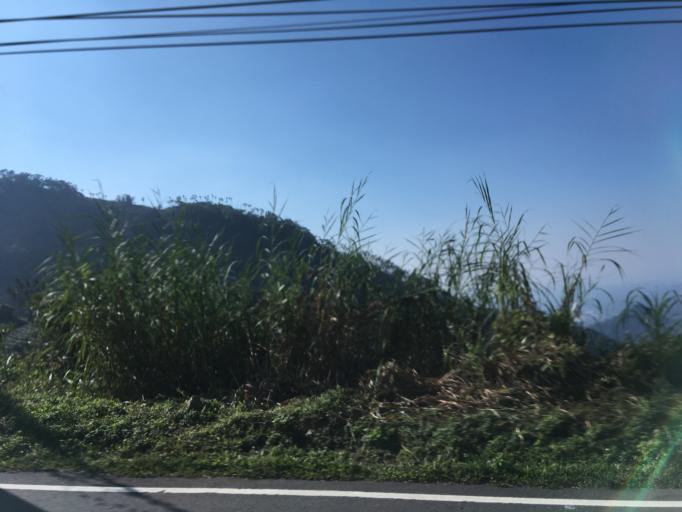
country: TW
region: Taiwan
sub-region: Chiayi
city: Jiayi Shi
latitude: 23.4241
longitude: 120.6430
